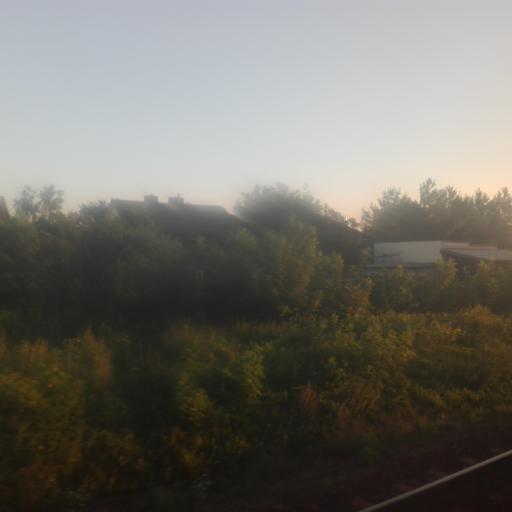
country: PL
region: Masovian Voivodeship
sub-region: Powiat warszawski zachodni
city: Bieniewice
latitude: 52.1899
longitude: 20.5258
